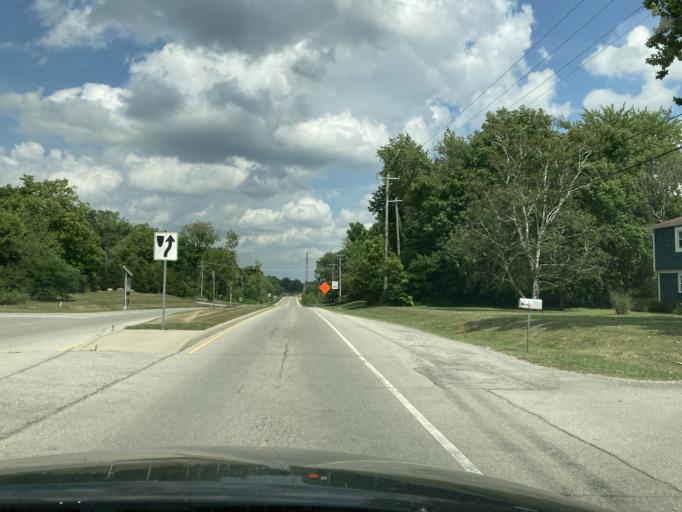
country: US
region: Indiana
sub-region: Boone County
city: Zionsville
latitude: 39.9987
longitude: -86.2465
